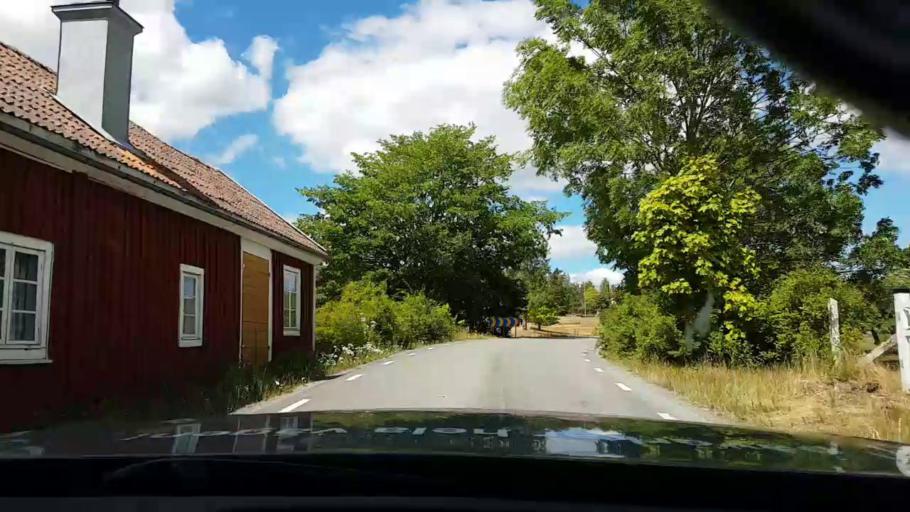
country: SE
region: Kalmar
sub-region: Vasterviks Kommun
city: Forserum
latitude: 58.0086
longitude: 16.5790
